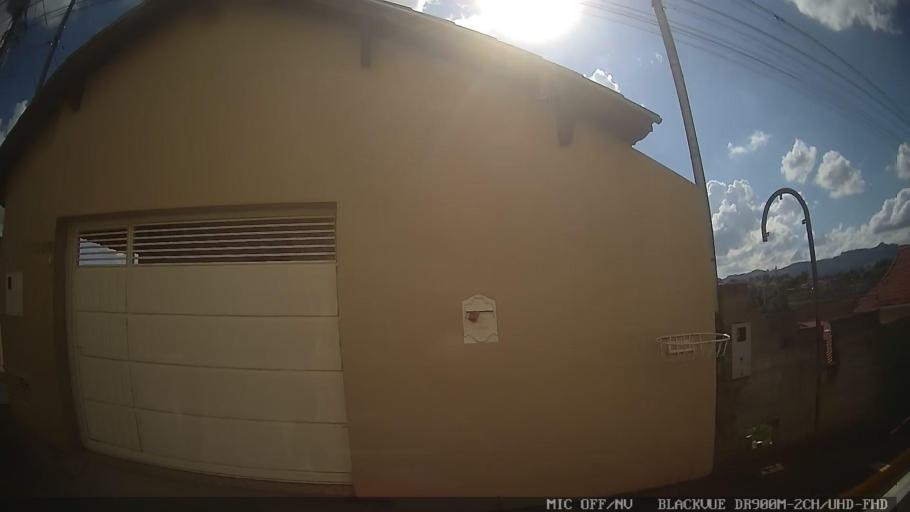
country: BR
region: Minas Gerais
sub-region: Extrema
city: Extrema
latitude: -22.8603
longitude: -46.3289
